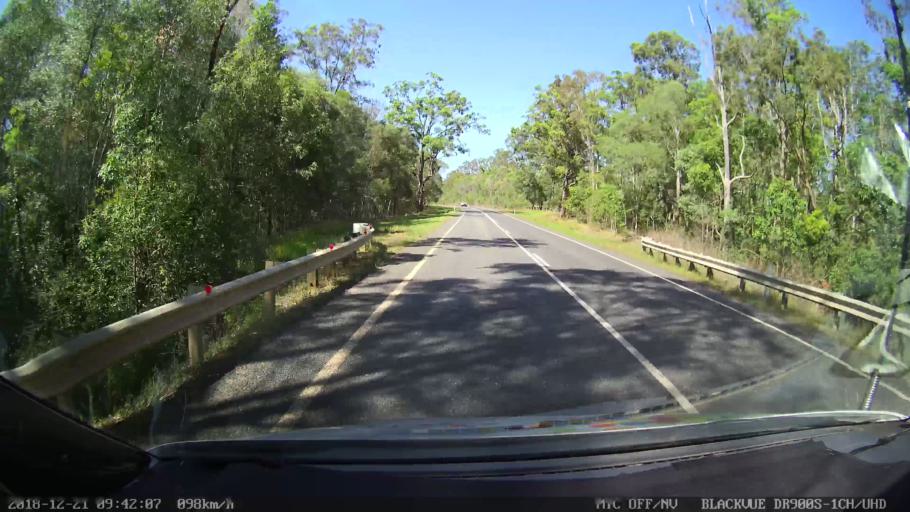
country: AU
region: New South Wales
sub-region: Clarence Valley
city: Grafton
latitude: -29.5926
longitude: 152.9499
